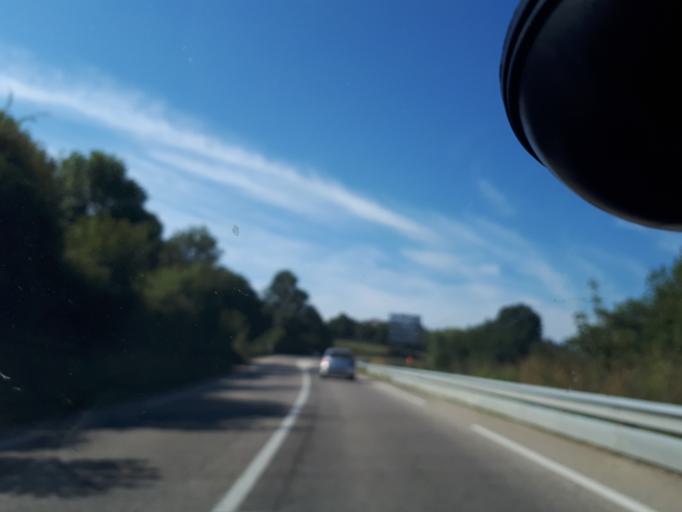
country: FR
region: Rhone-Alpes
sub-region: Departement de l'Isere
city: Maubec
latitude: 45.5400
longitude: 5.2325
